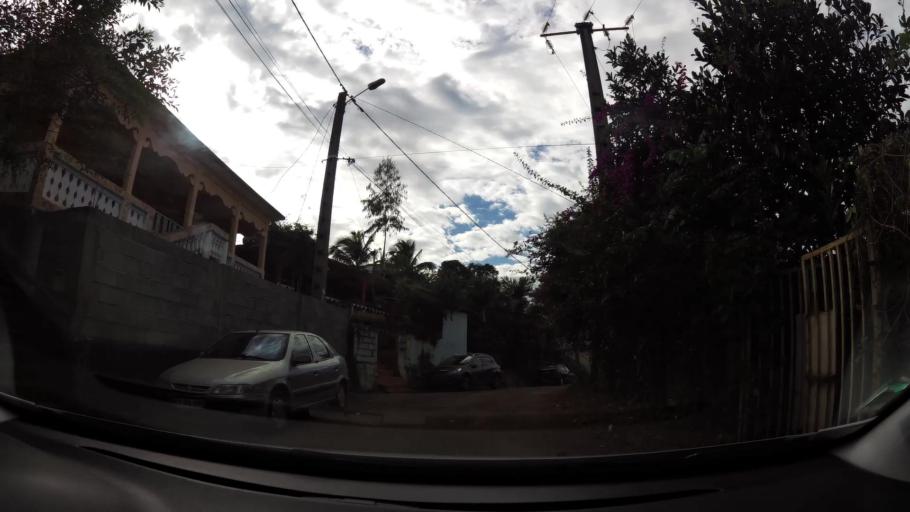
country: YT
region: Ouangani
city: Ouangani
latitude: -12.8384
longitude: 45.1329
